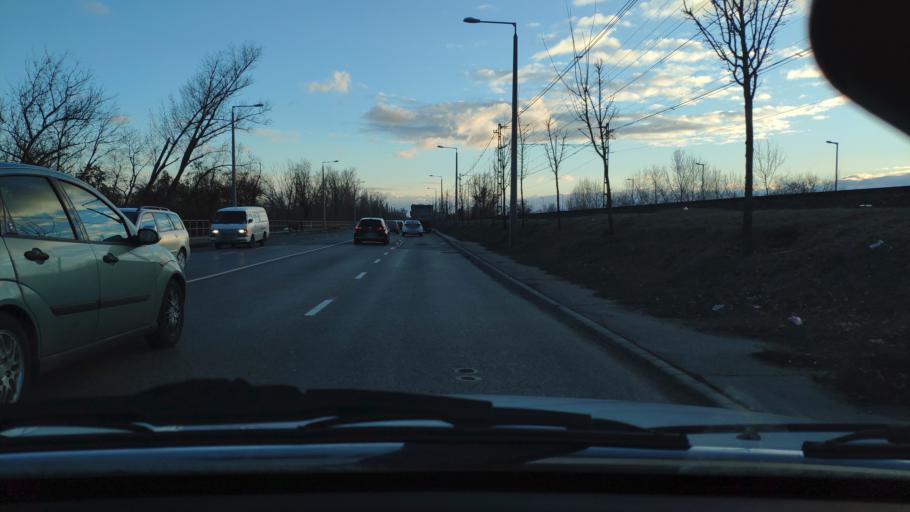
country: HU
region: Budapest
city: Budapest XXI. keruelet
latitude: 47.4561
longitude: 19.0713
